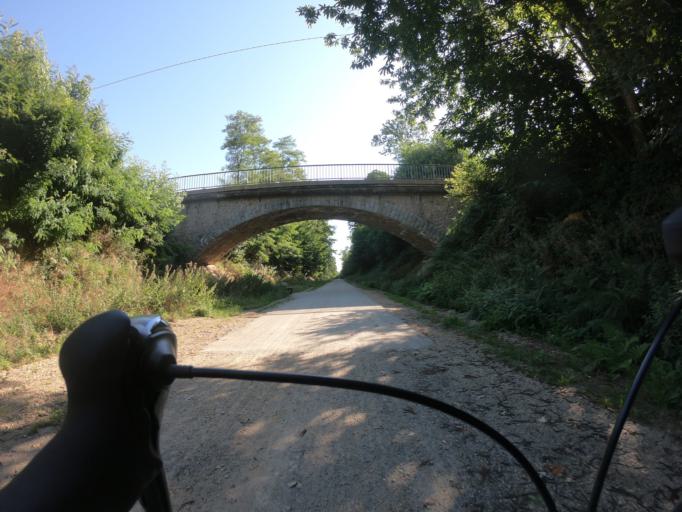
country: FR
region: Lower Normandy
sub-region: Departement de la Manche
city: Parigny
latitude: 48.6078
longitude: -1.0304
